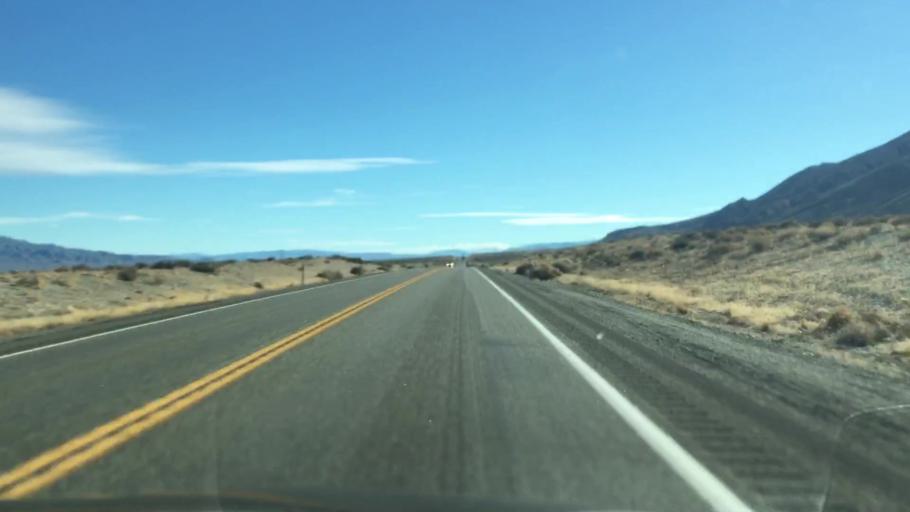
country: US
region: Nevada
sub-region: Mineral County
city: Hawthorne
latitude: 38.8163
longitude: -118.7674
